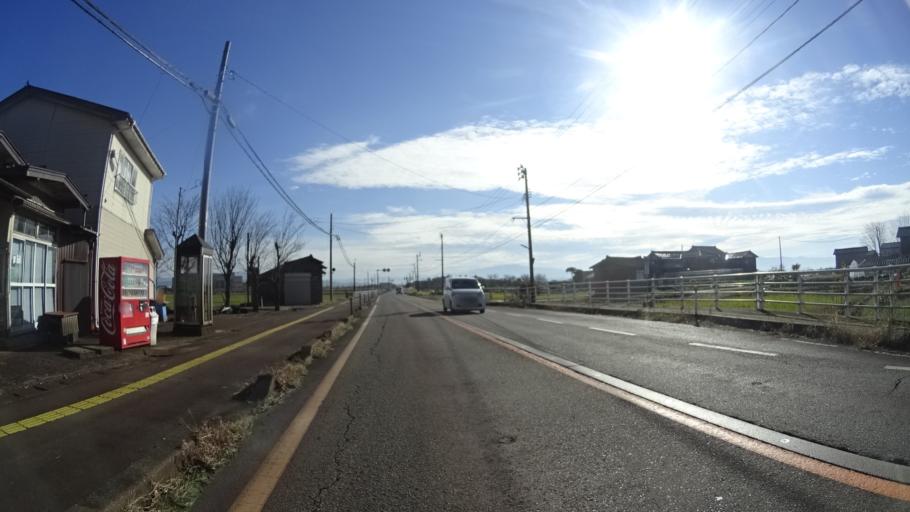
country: JP
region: Niigata
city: Mitsuke
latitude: 37.5542
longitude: 138.8577
